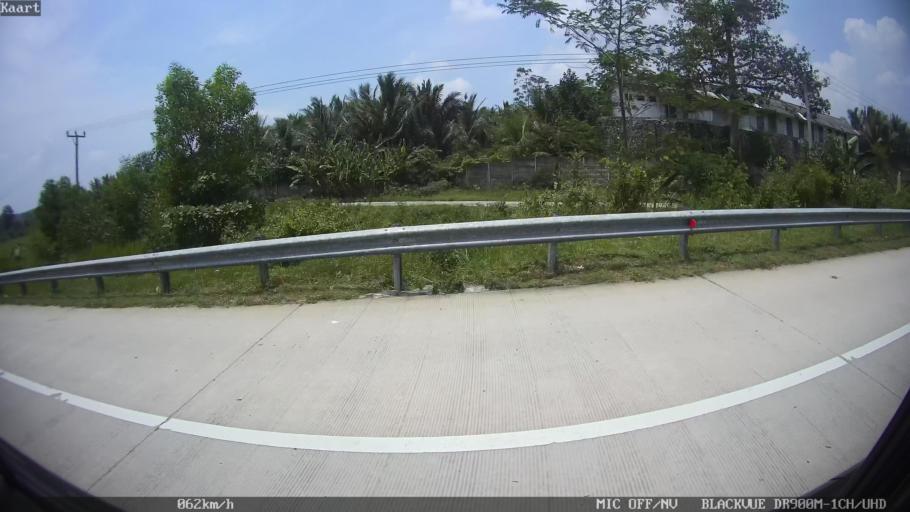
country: ID
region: Lampung
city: Natar
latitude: -5.2814
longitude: 105.1966
